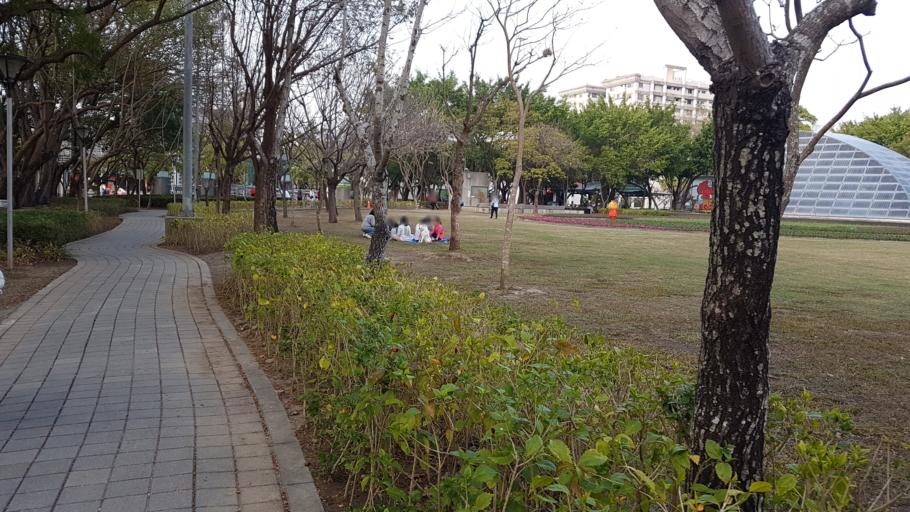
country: TW
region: Taiwan
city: Xinying
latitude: 23.3098
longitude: 120.3150
